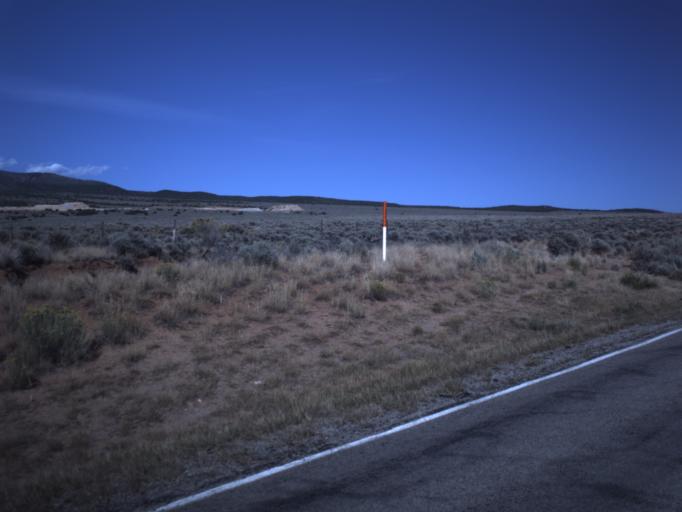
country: US
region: Utah
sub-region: Grand County
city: Moab
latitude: 38.3165
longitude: -109.3126
